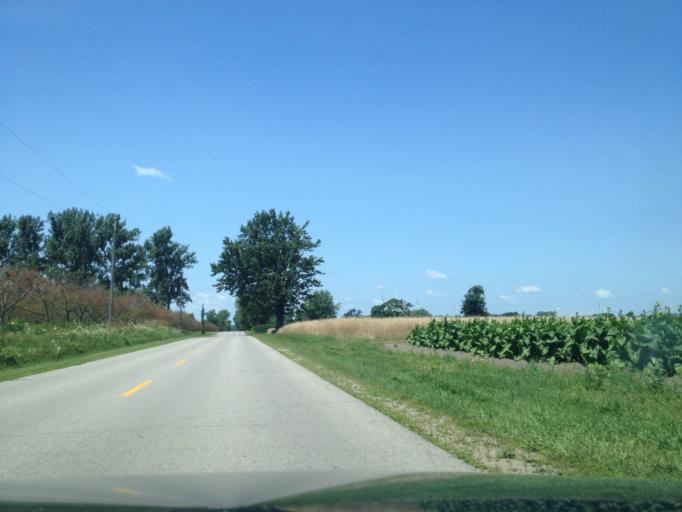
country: CA
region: Ontario
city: Aylmer
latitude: 42.6135
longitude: -80.6956
